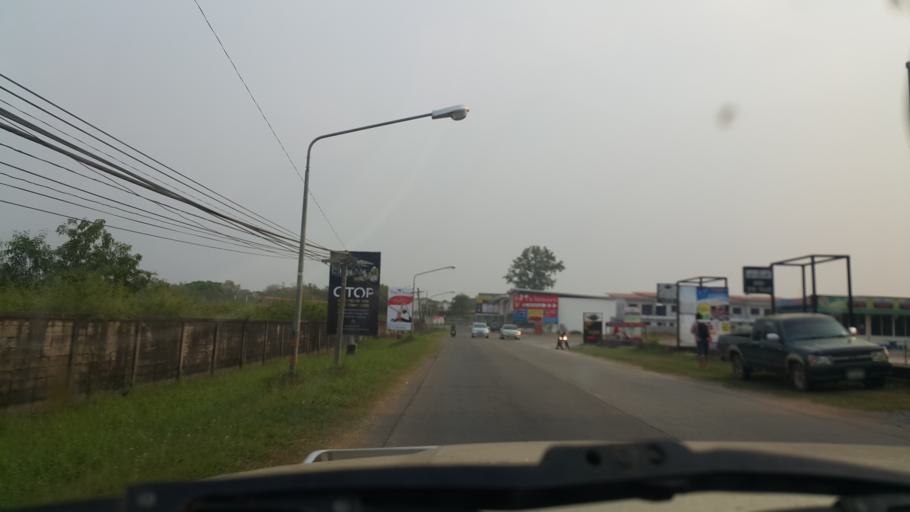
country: TH
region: Changwat Udon Thani
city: Udon Thani
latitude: 17.3958
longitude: 102.7711
